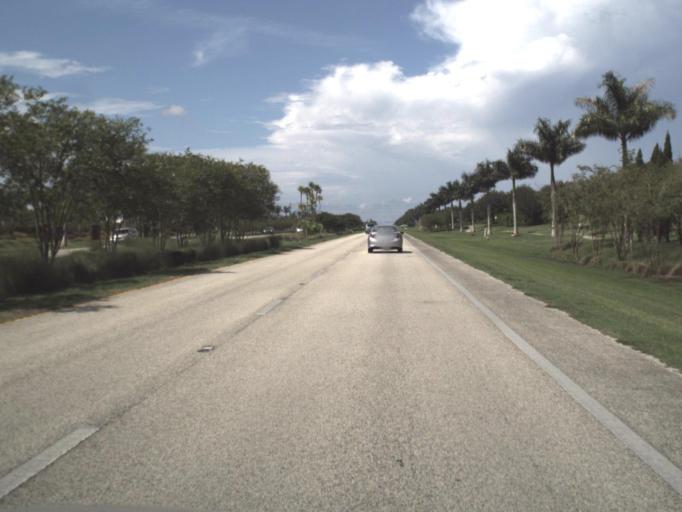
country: US
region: Florida
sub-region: Sarasota County
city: Plantation
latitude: 27.0497
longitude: -82.3446
